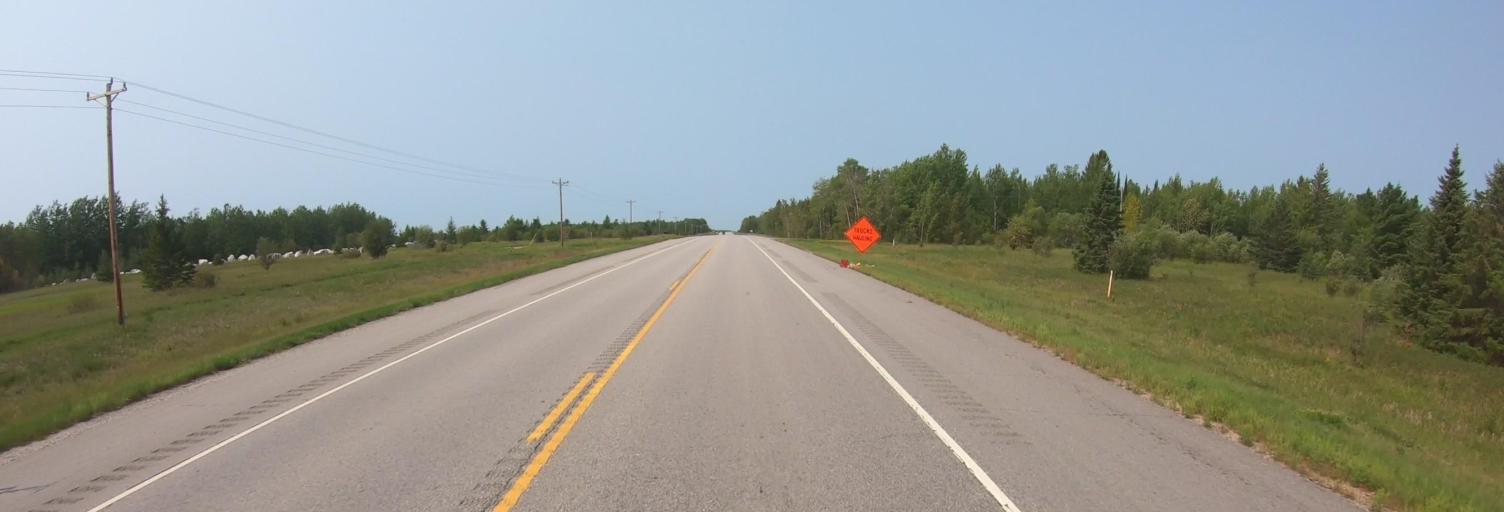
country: CA
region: Ontario
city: Fort Frances
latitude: 48.4102
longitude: -93.1571
